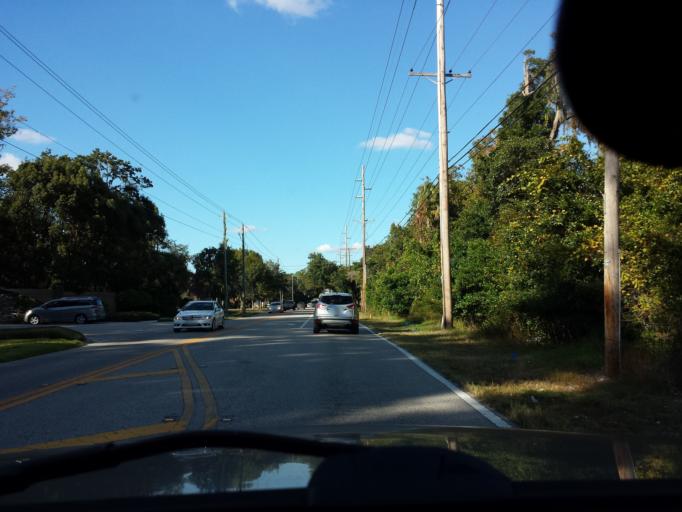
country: US
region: Florida
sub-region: Hillsborough County
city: Bloomingdale
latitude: 27.8600
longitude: -82.2692
